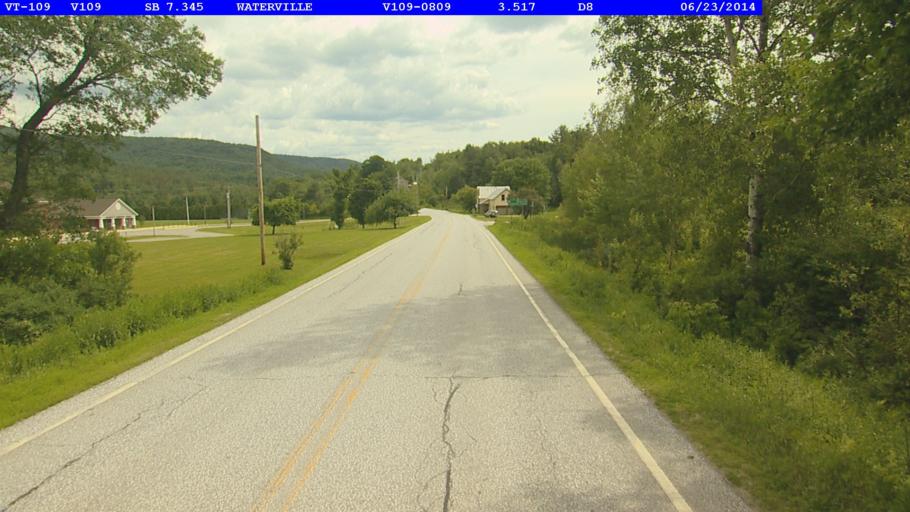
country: US
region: Vermont
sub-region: Lamoille County
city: Johnson
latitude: 44.7281
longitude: -72.7493
